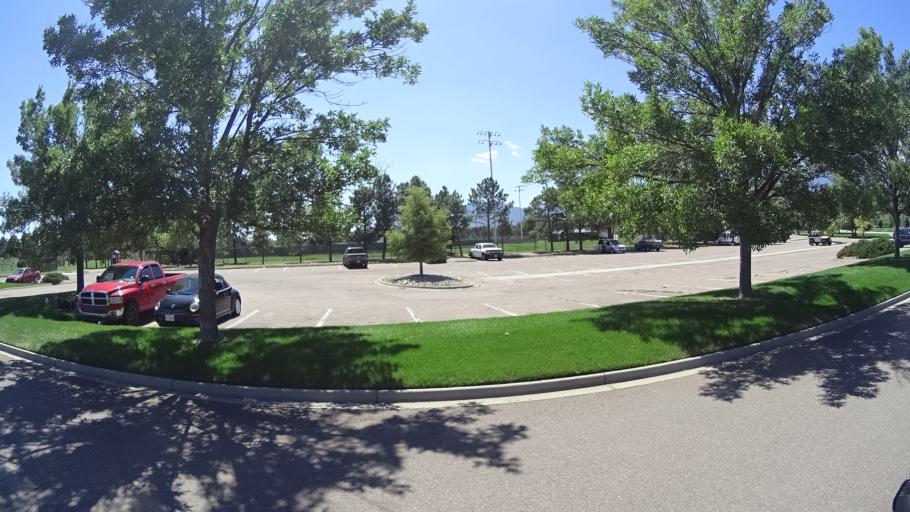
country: US
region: Colorado
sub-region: El Paso County
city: Colorado Springs
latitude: 38.8322
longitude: -104.8002
